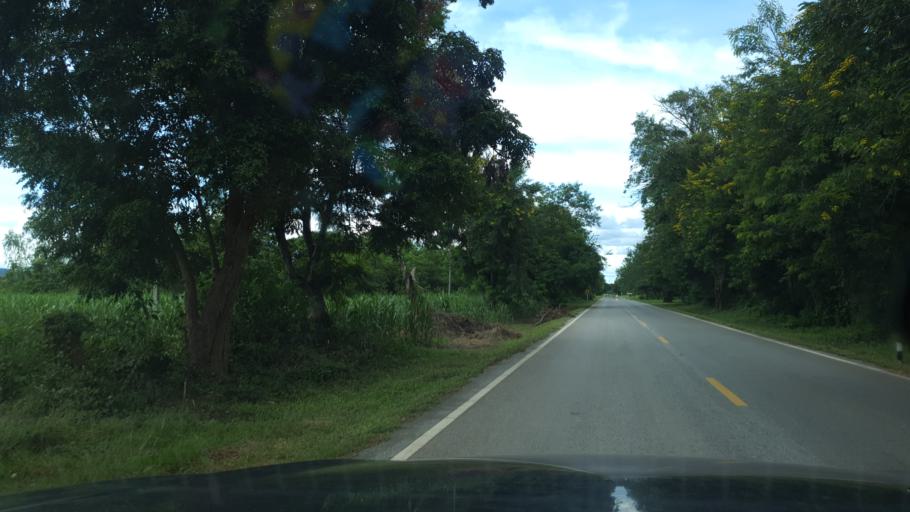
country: TH
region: Sukhothai
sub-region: Amphoe Si Satchanalai
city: Si Satchanalai
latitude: 17.4787
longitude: 99.7537
